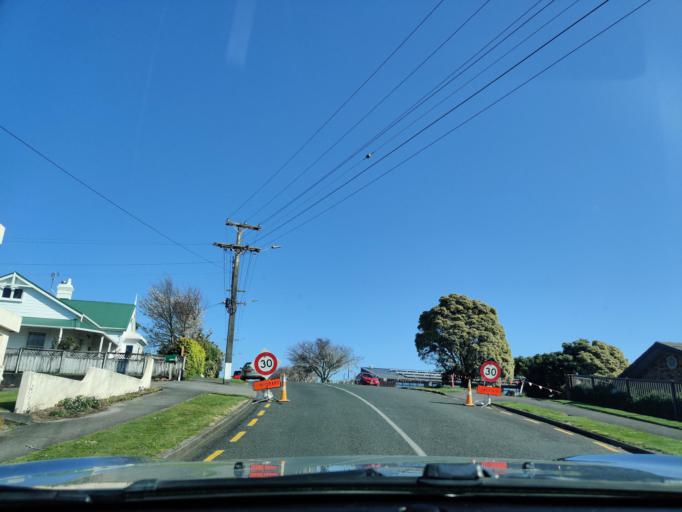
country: NZ
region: Taranaki
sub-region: New Plymouth District
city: New Plymouth
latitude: -39.0702
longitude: 174.0571
